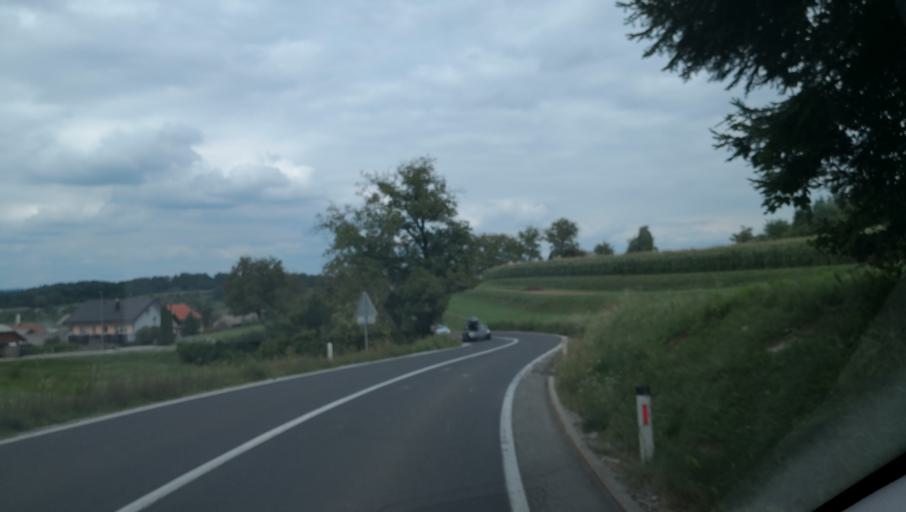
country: SI
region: Novo Mesto
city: Novo Mesto
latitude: 45.7655
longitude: 15.1966
